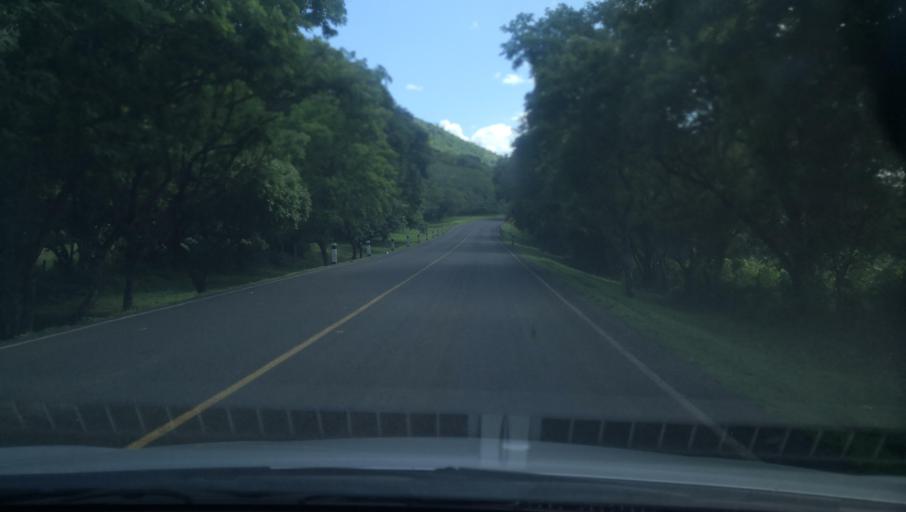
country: NI
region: Madriz
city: Somoto
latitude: 13.4657
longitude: -86.6364
